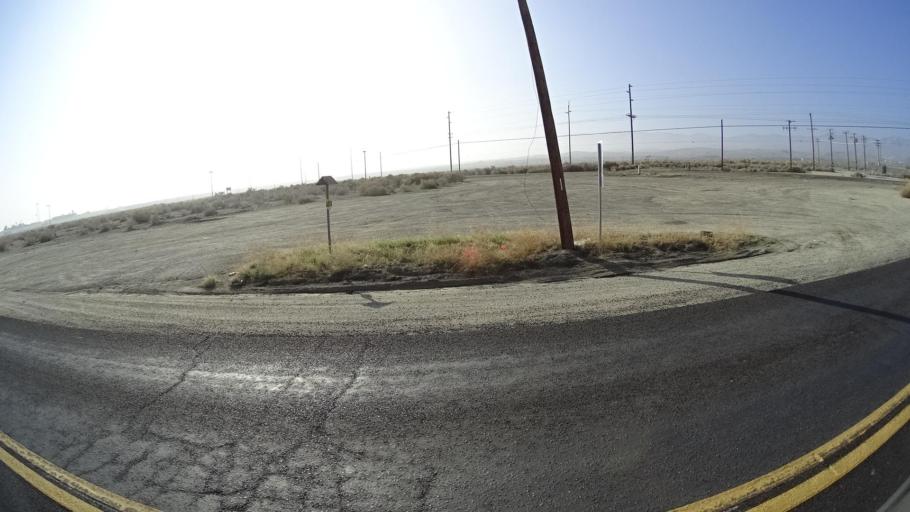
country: US
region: California
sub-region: Kern County
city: Taft Heights
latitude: 35.1801
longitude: -119.5264
